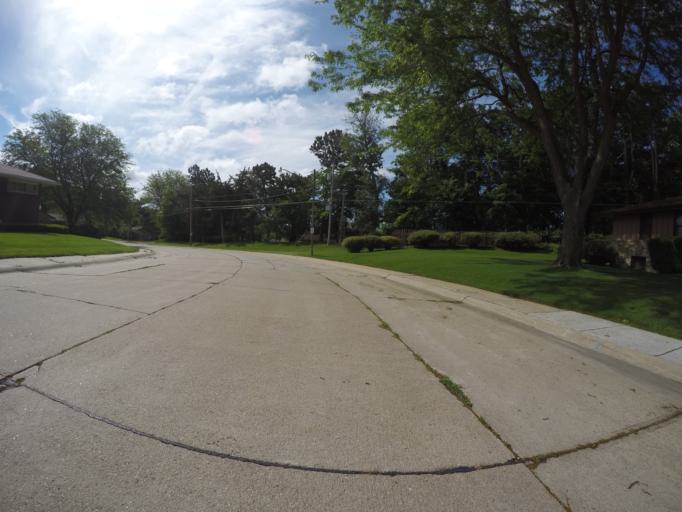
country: US
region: Nebraska
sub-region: Buffalo County
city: Kearney
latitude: 40.7070
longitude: -99.0964
